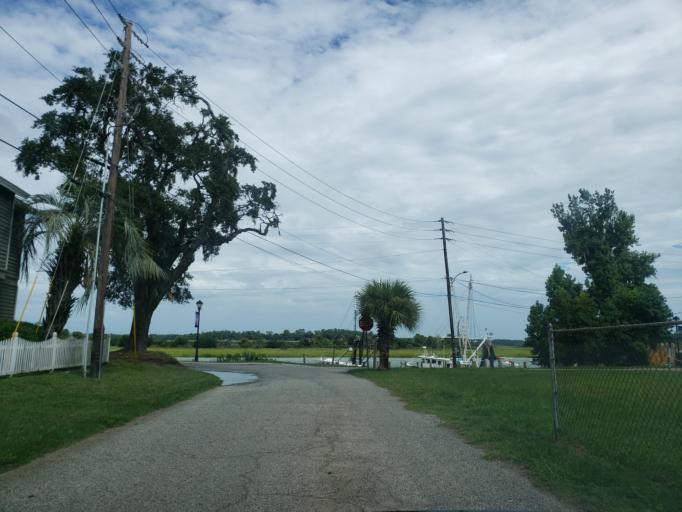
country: US
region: Georgia
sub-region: Chatham County
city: Thunderbolt
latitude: 32.0273
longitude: -81.0504
